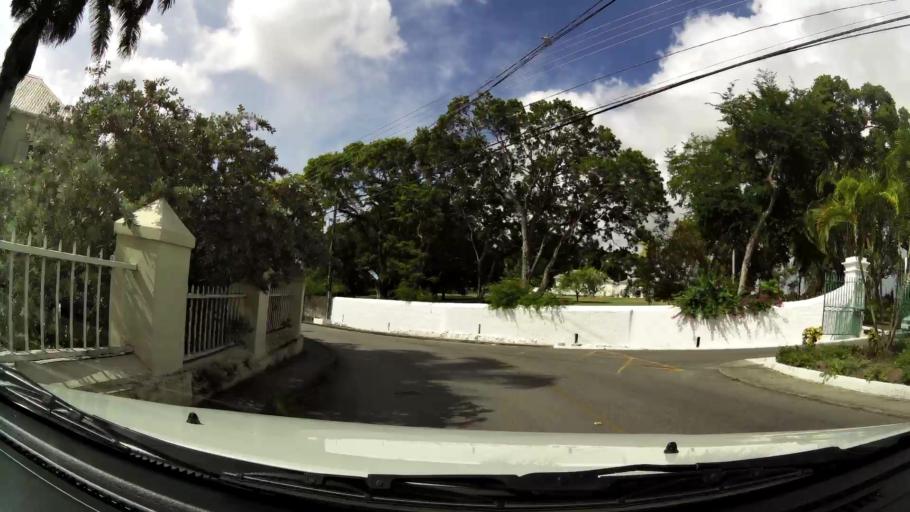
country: BB
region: Saint Michael
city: Bridgetown
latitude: 13.1004
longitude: -59.6001
